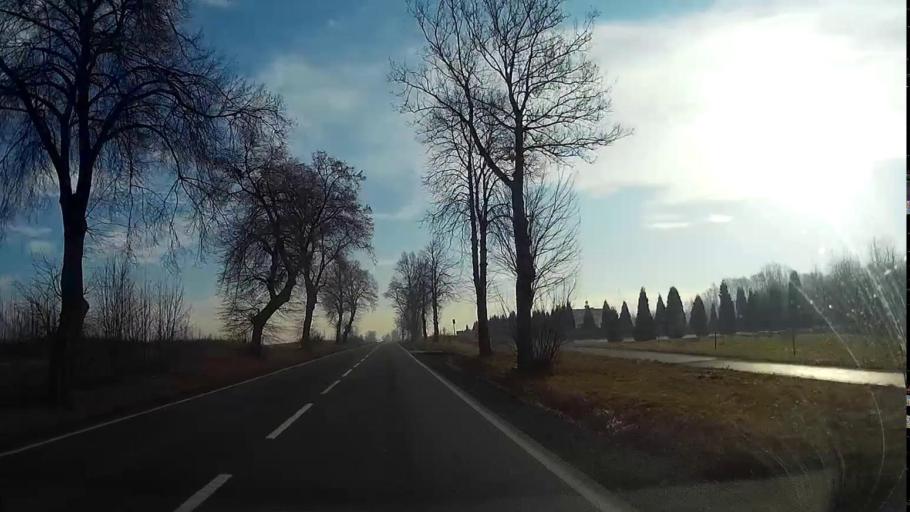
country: PL
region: Lesser Poland Voivodeship
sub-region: Powiat chrzanowski
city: Kwaczala
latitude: 50.0625
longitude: 19.4981
